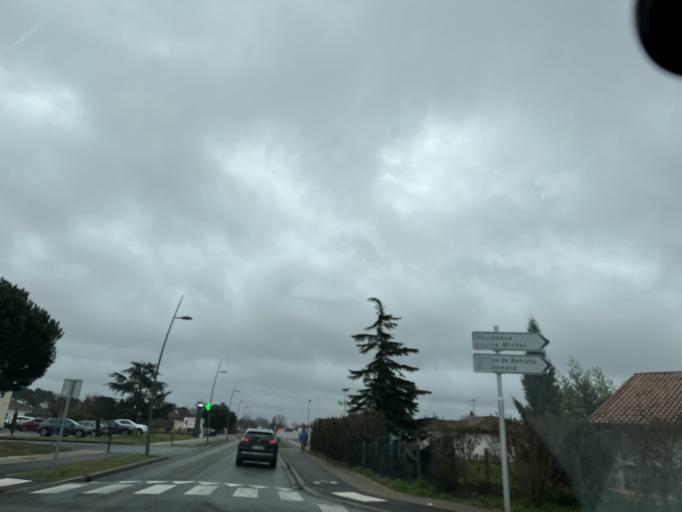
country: FR
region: Aquitaine
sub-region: Departement de la Gironde
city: Lesparre-Medoc
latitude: 45.3026
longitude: -0.9349
